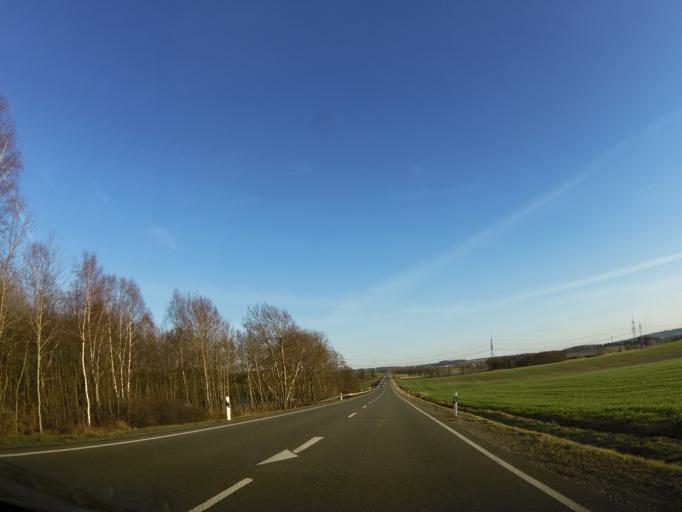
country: DE
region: Thuringia
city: Pormitz
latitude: 50.6254
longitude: 11.8148
